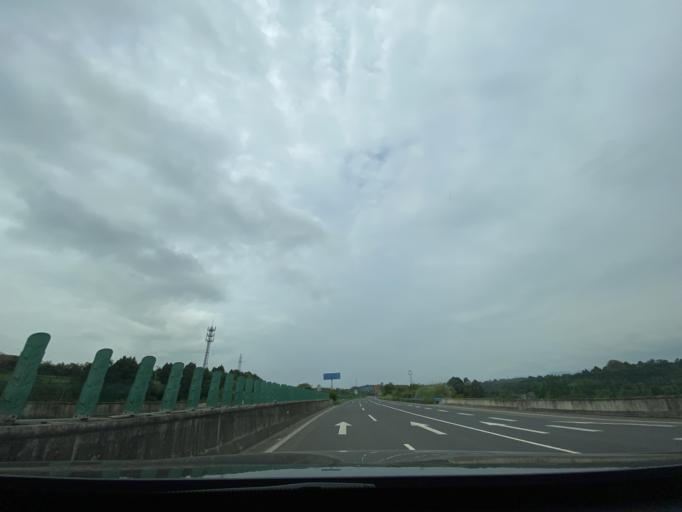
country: CN
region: Sichuan
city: Jiancheng
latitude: 30.4273
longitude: 104.3996
